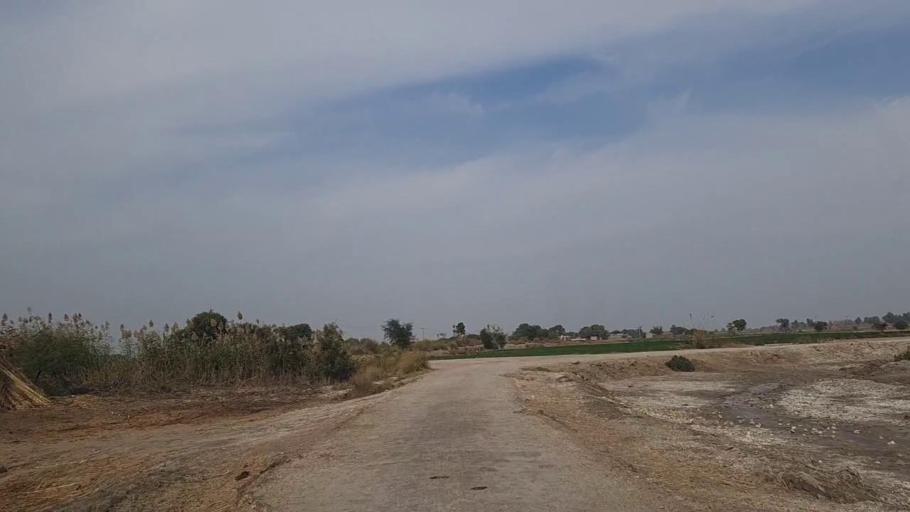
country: PK
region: Sindh
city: Daur
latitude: 26.4779
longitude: 68.4024
